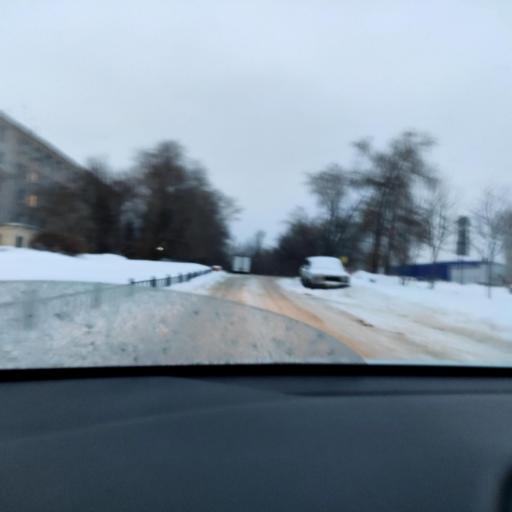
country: RU
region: Tatarstan
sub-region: Gorod Kazan'
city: Kazan
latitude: 55.8441
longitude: 49.0710
